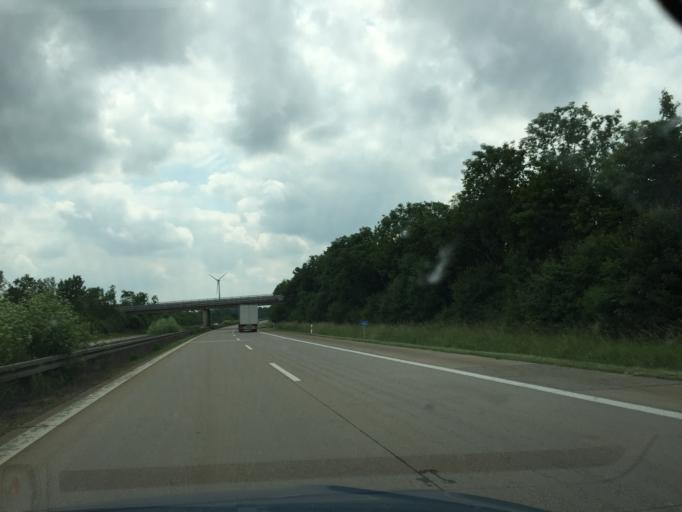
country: DE
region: Bavaria
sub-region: Regierungsbezirk Mittelfranken
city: Schopfloch
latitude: 49.1498
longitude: 10.2657
